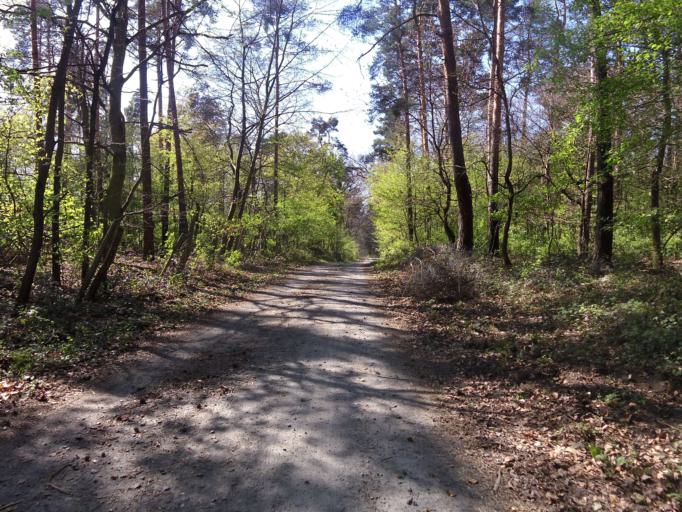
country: DE
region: Hesse
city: Raunheim
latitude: 50.0176
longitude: 8.4780
